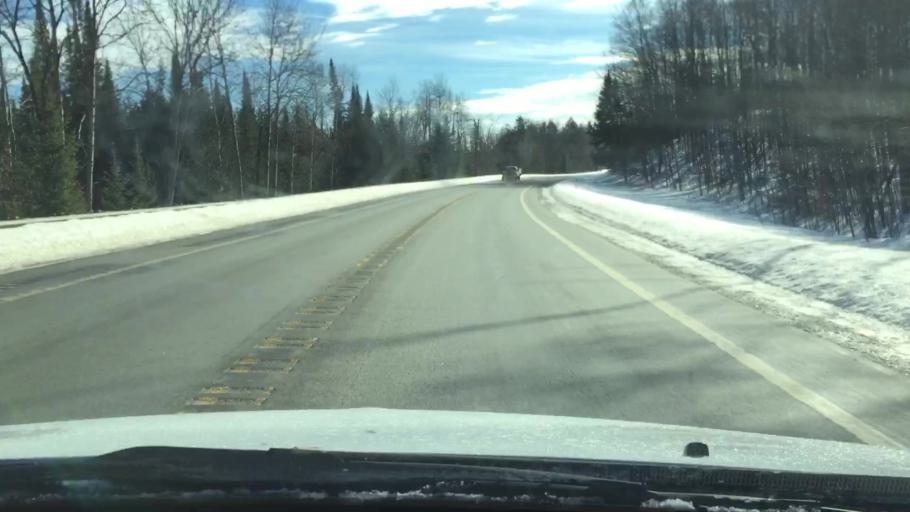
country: US
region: Michigan
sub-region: Antrim County
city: Mancelona
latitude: 44.9974
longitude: -85.0616
